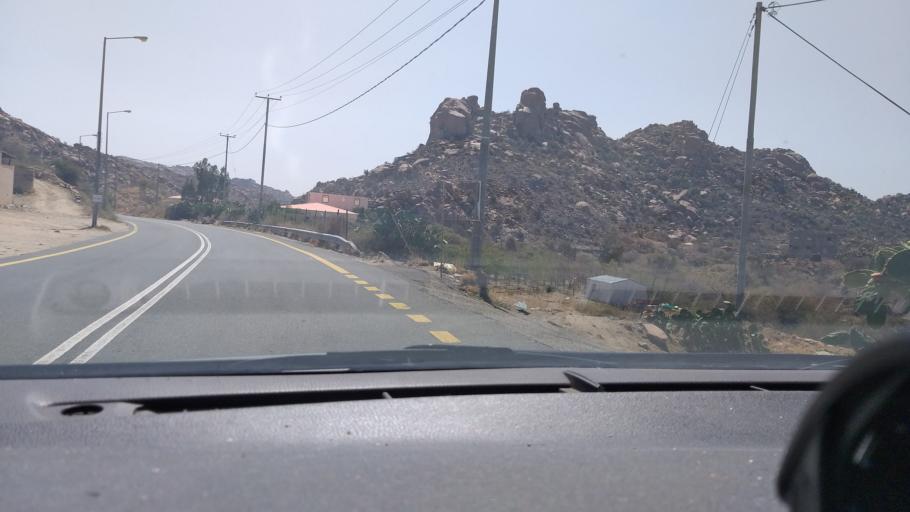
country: SA
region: Makkah
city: Ash Shafa
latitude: 21.0919
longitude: 40.3528
